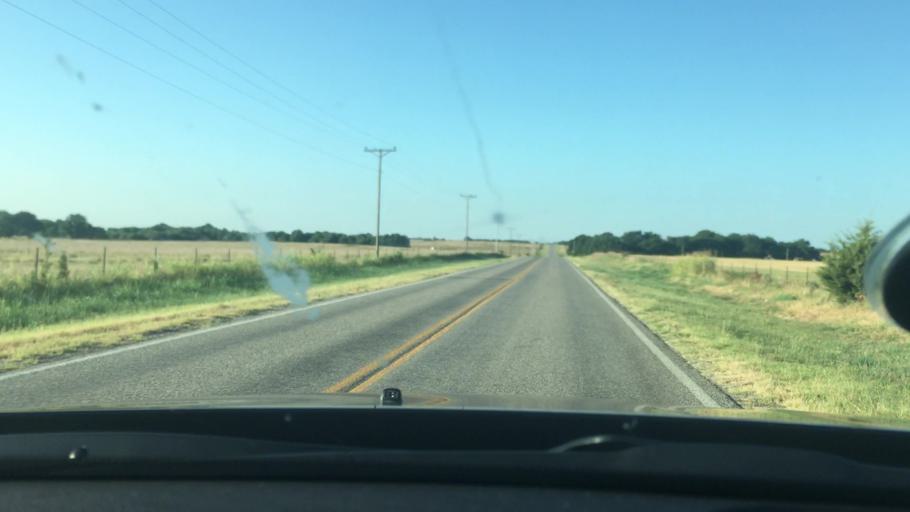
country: US
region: Oklahoma
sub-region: Murray County
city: Sulphur
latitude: 34.5928
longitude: -96.8449
